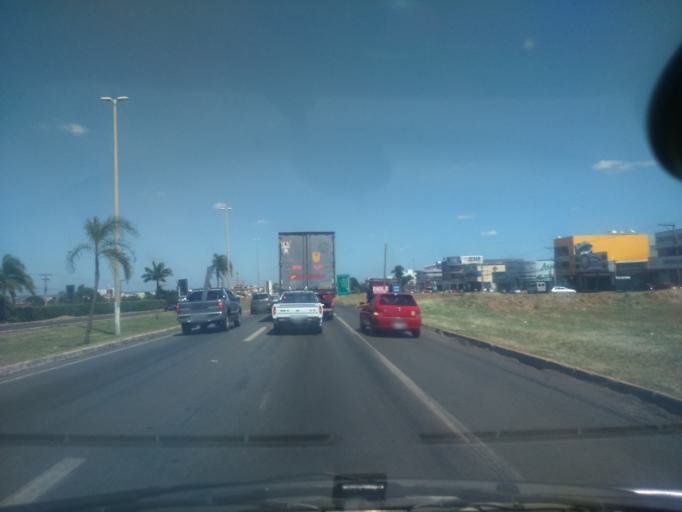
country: BR
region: Goias
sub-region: Luziania
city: Luziania
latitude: -16.0631
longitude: -47.9837
